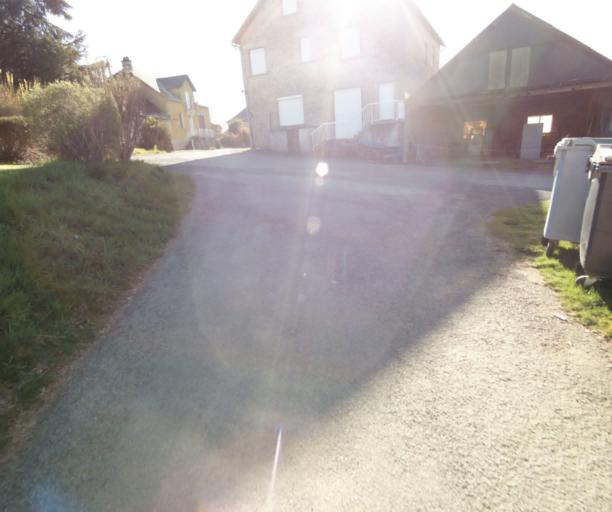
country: FR
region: Limousin
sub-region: Departement de la Correze
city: Seilhac
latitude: 45.3961
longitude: 1.7634
